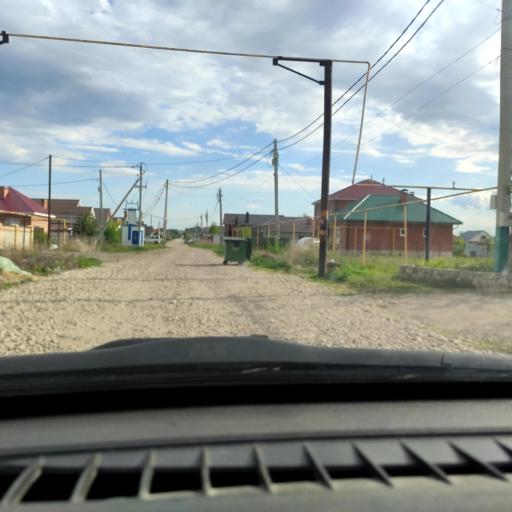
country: RU
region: Samara
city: Tol'yatti
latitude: 53.5665
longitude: 49.4078
